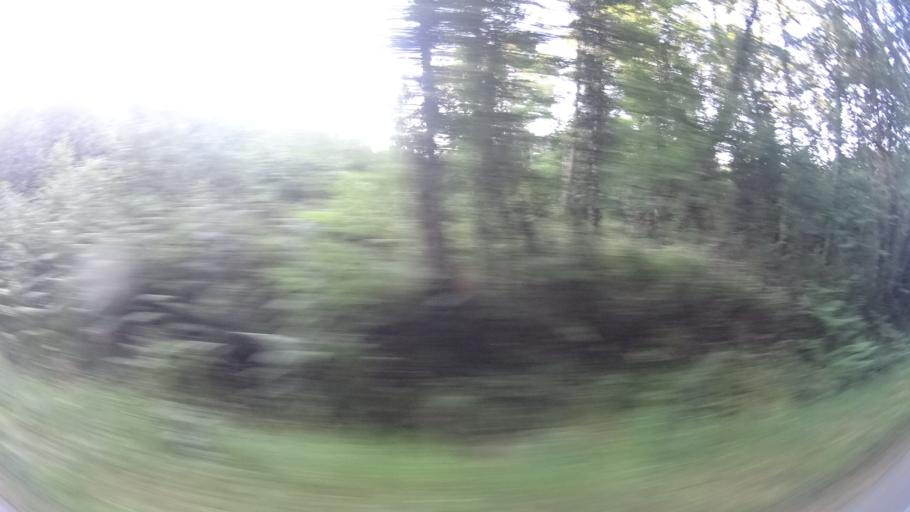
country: FR
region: Brittany
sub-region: Departement d'Ille-et-Vilaine
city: Saint-Just
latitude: 47.7189
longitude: -1.9216
